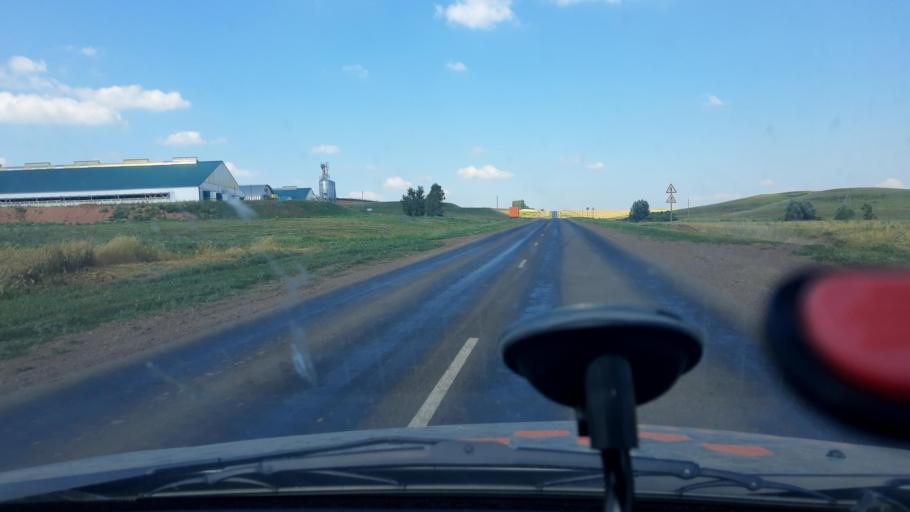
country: RU
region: Bashkortostan
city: Chekmagush
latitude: 55.0619
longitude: 54.6269
